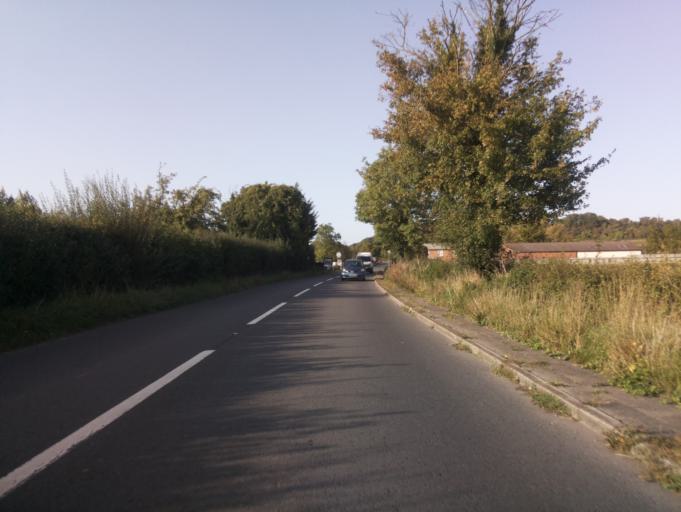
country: GB
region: England
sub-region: Gloucestershire
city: Gloucester
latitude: 51.9305
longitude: -2.2942
